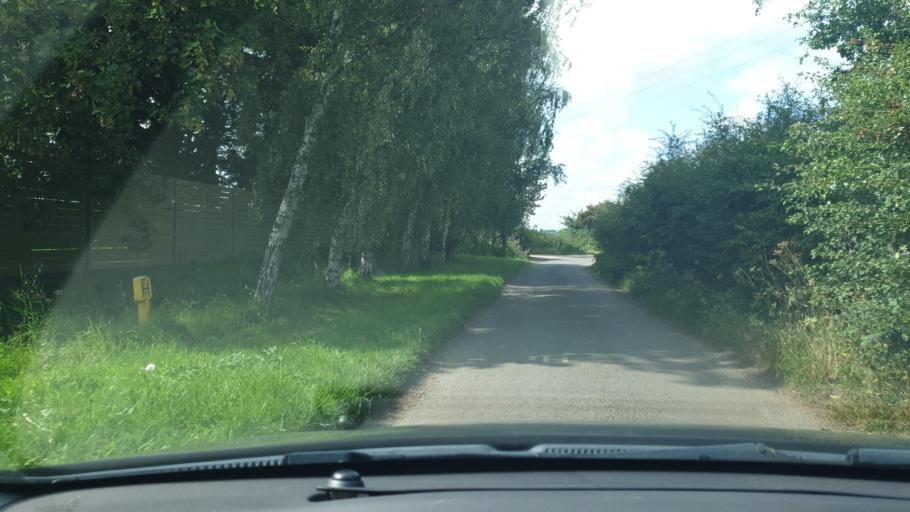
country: GB
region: England
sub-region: Suffolk
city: East Bergholt
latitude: 51.9183
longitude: 0.9997
